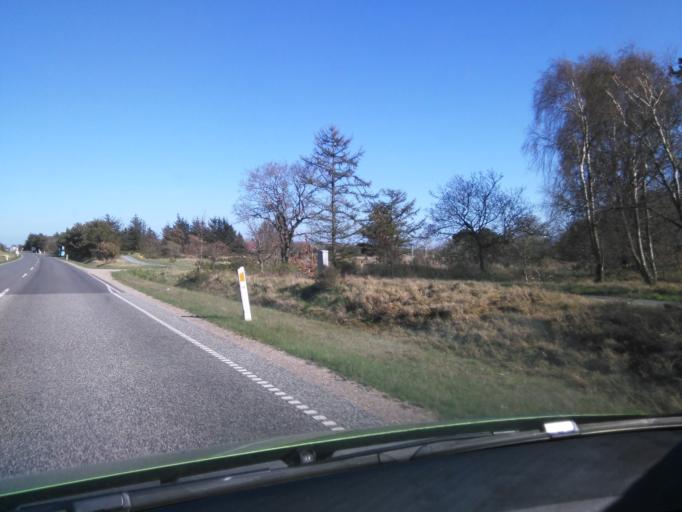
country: DK
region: South Denmark
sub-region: Varde Kommune
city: Oksbol
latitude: 55.6152
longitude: 8.2460
